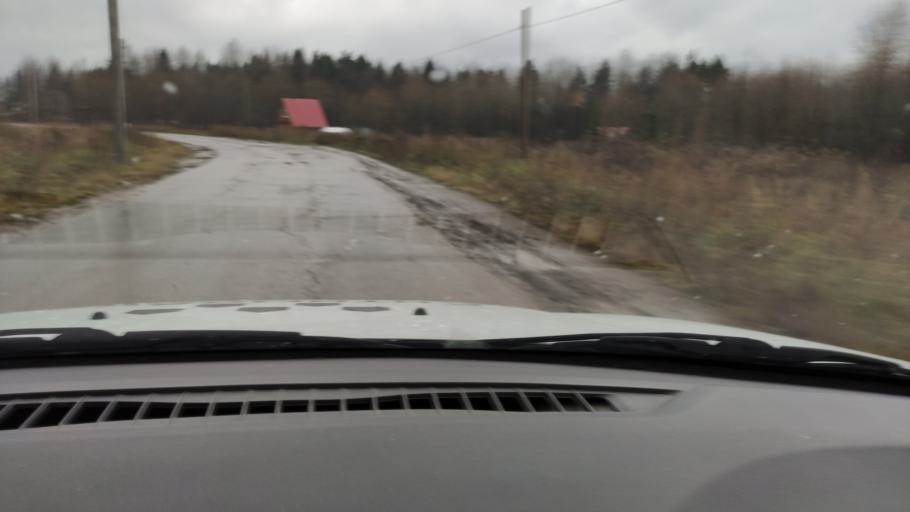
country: RU
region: Perm
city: Sylva
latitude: 58.0396
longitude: 56.7463
